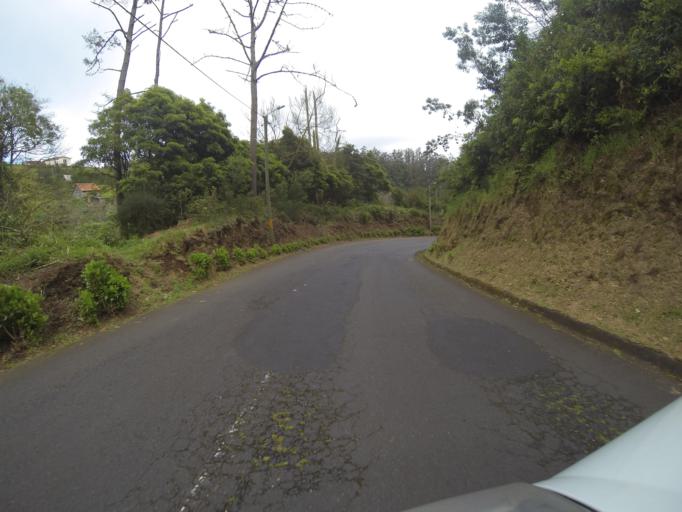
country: PT
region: Madeira
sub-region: Santa Cruz
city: Santa Cruz
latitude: 32.7377
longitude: -16.8207
